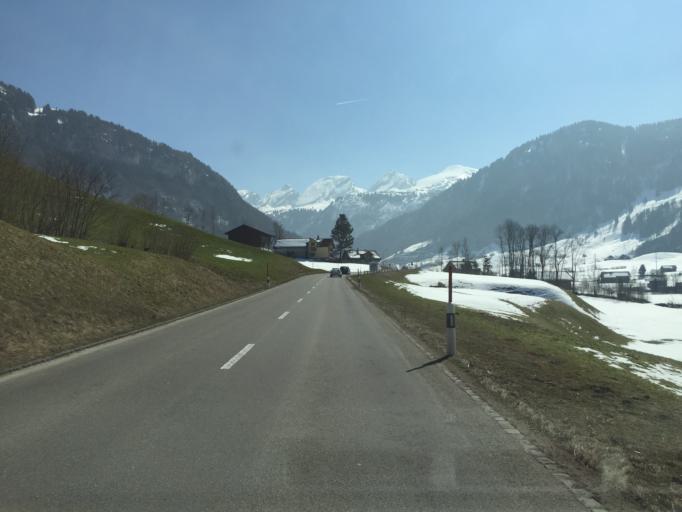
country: CH
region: Saint Gallen
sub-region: Wahlkreis Toggenburg
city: Krummenau
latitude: 47.2071
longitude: 9.2196
